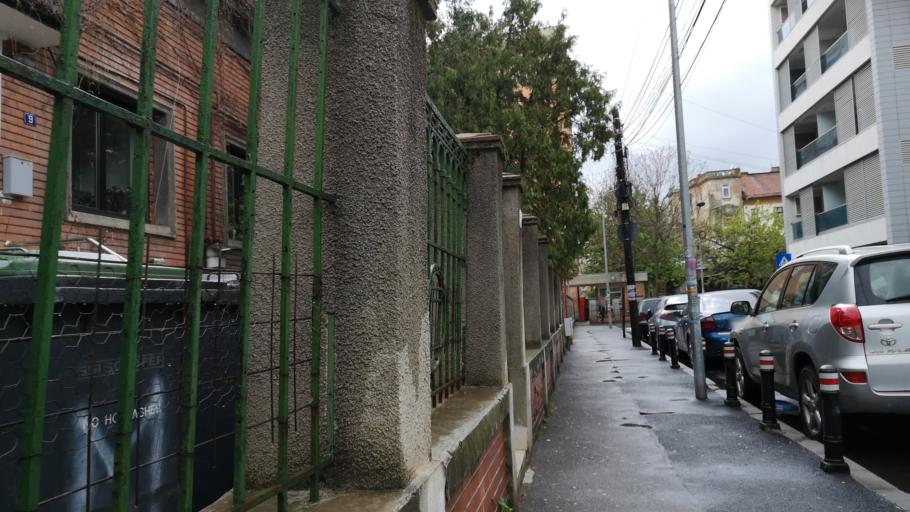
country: RO
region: Bucuresti
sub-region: Municipiul Bucuresti
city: Bucuresti
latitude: 44.4464
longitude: 26.0881
